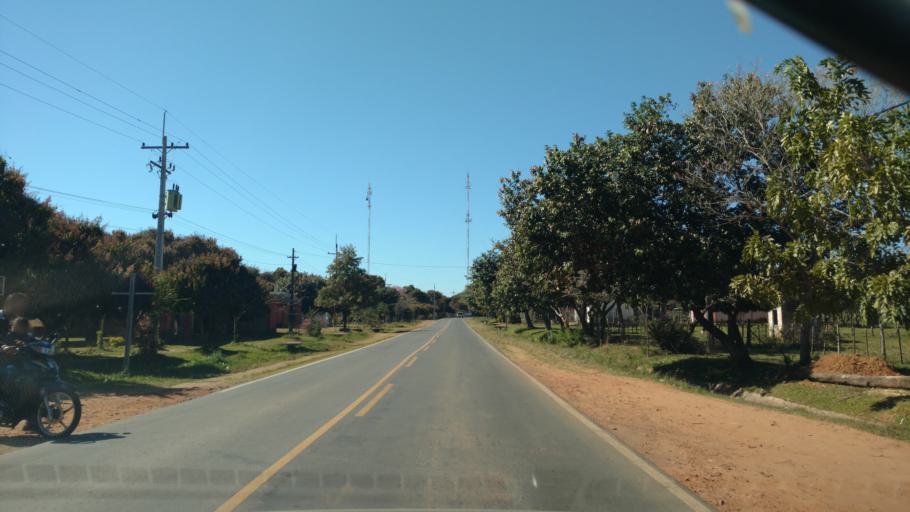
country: PY
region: Paraguari
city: Pirayu
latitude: -25.4741
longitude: -57.2516
